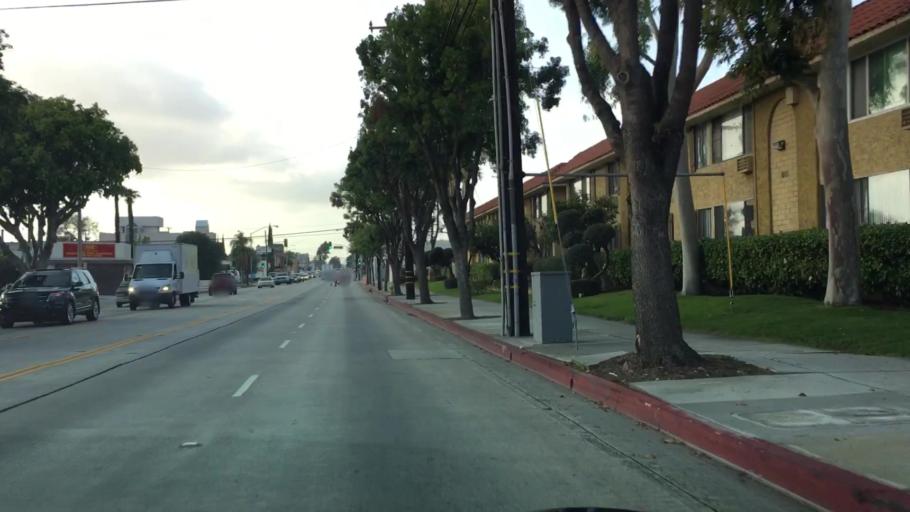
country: US
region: California
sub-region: Los Angeles County
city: Montebello
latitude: 34.0165
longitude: -118.1022
